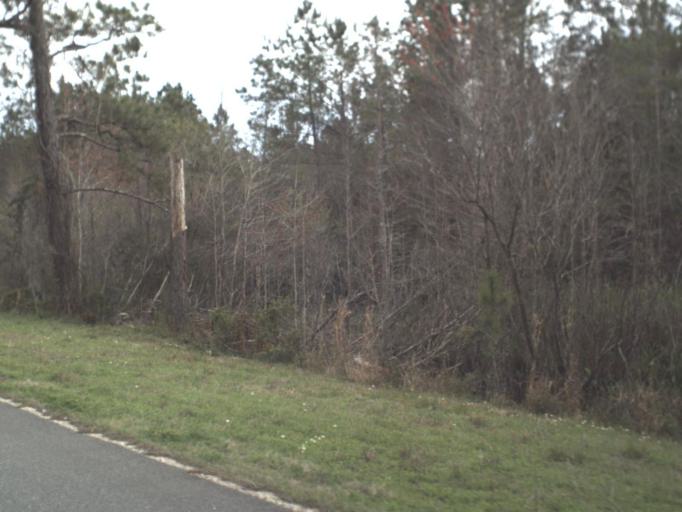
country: US
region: Florida
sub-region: Leon County
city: Woodville
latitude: 30.1835
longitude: -84.0151
